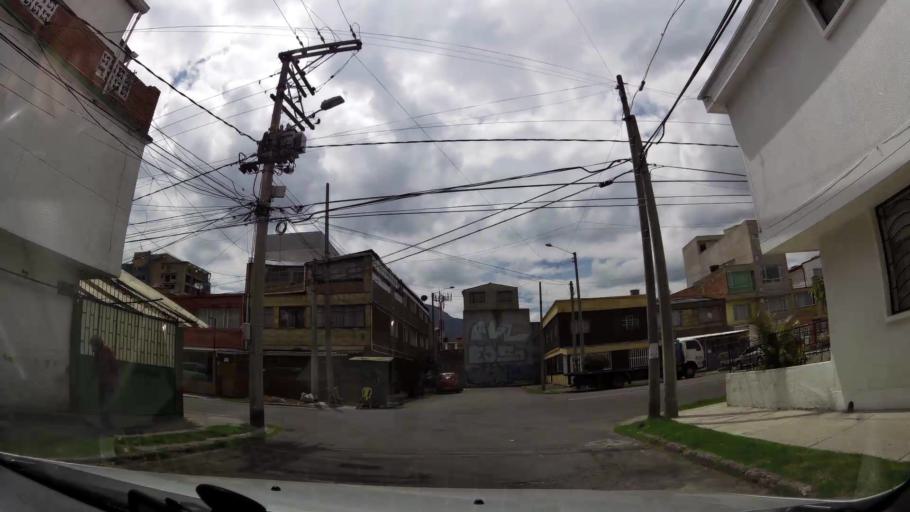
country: CO
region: Bogota D.C.
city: Bogota
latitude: 4.5993
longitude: -74.0969
